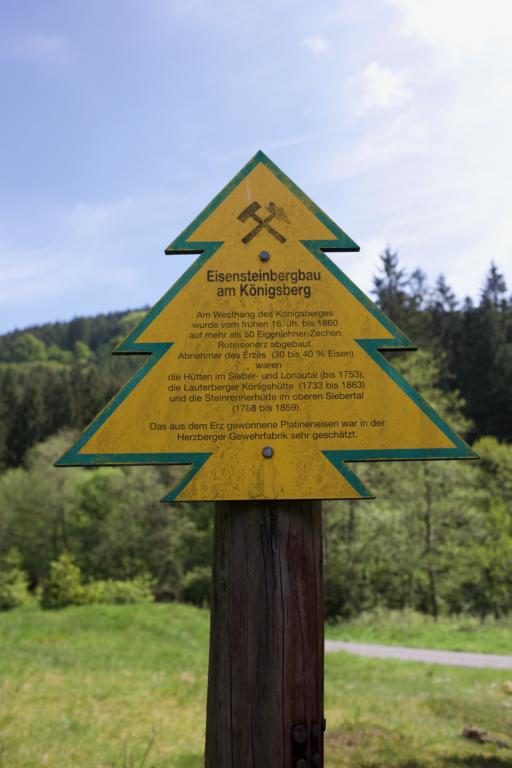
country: DE
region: Lower Saxony
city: Sankt Andreasberg
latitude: 51.7120
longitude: 10.4629
